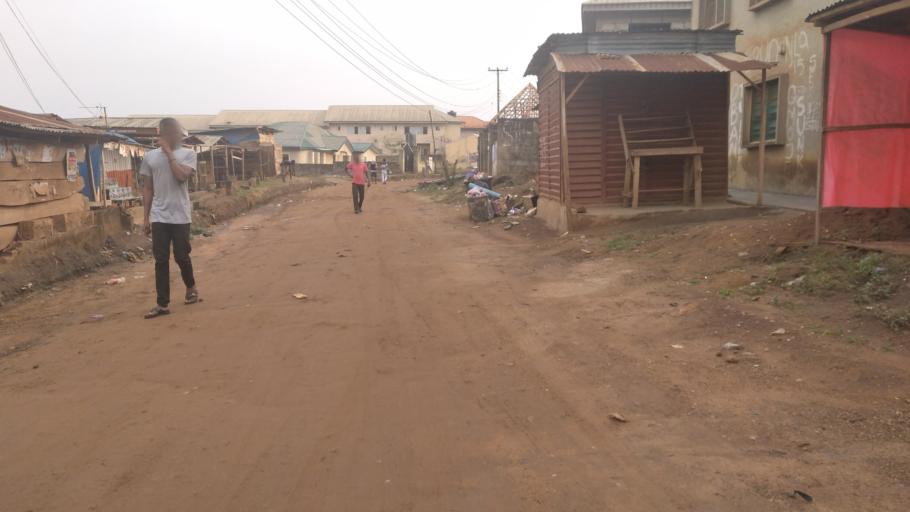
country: NG
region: Ondo
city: Akure
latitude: 7.2926
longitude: 5.1533
